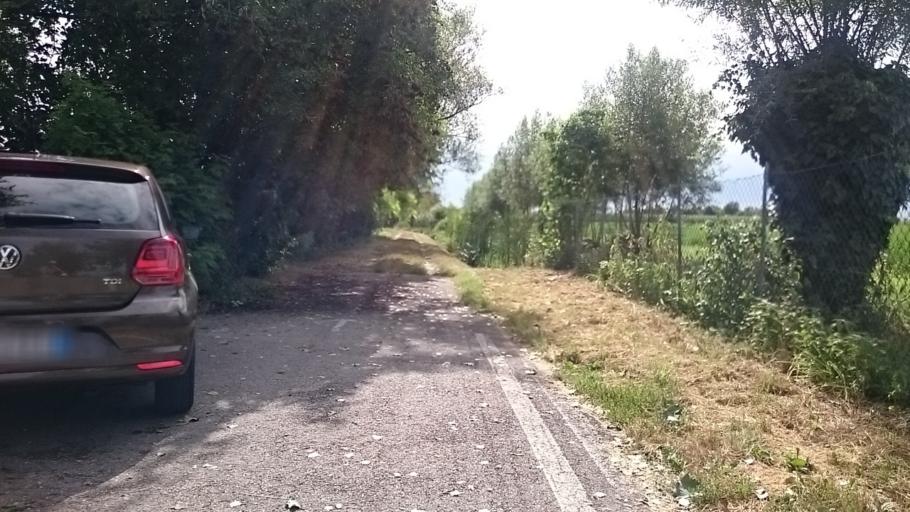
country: IT
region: Veneto
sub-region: Provincia di Padova
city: Bertipaglia
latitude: 45.3274
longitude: 11.8789
